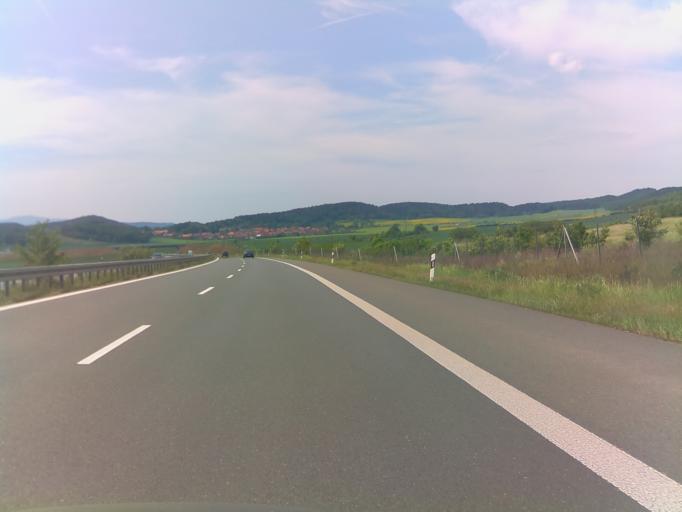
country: DE
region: Saxony-Anhalt
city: Westerhausen
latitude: 51.8173
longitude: 11.0767
